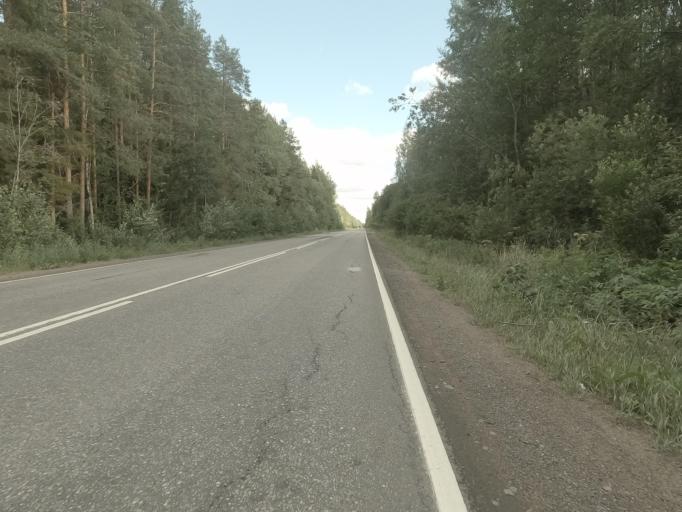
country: RU
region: Leningrad
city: Shcheglovo
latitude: 60.0058
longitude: 30.8639
